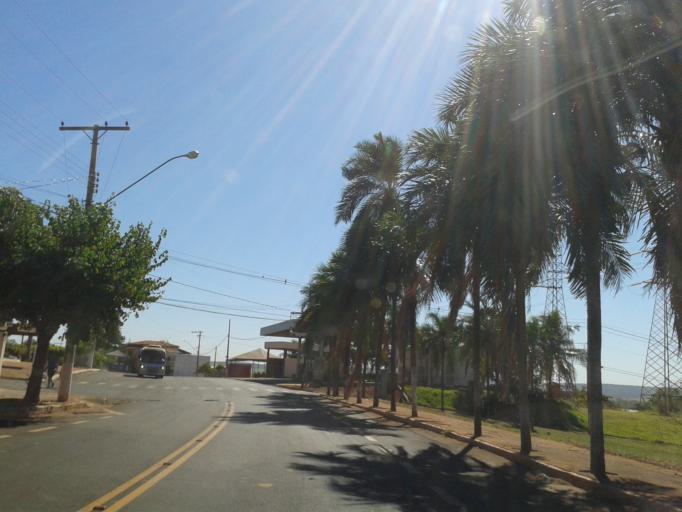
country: BR
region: Minas Gerais
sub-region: Capinopolis
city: Capinopolis
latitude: -18.5179
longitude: -49.4998
